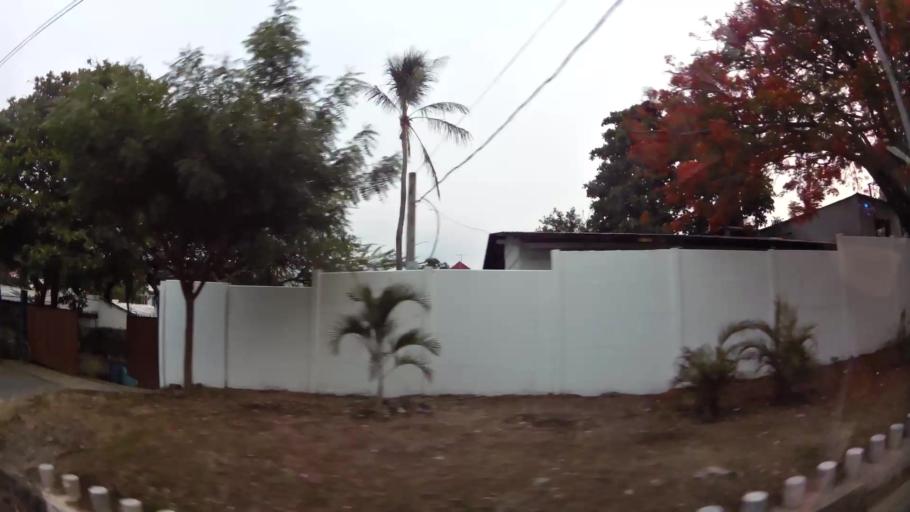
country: NI
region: Rivas
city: San Juan del Sur
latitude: 11.2621
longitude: -85.8796
